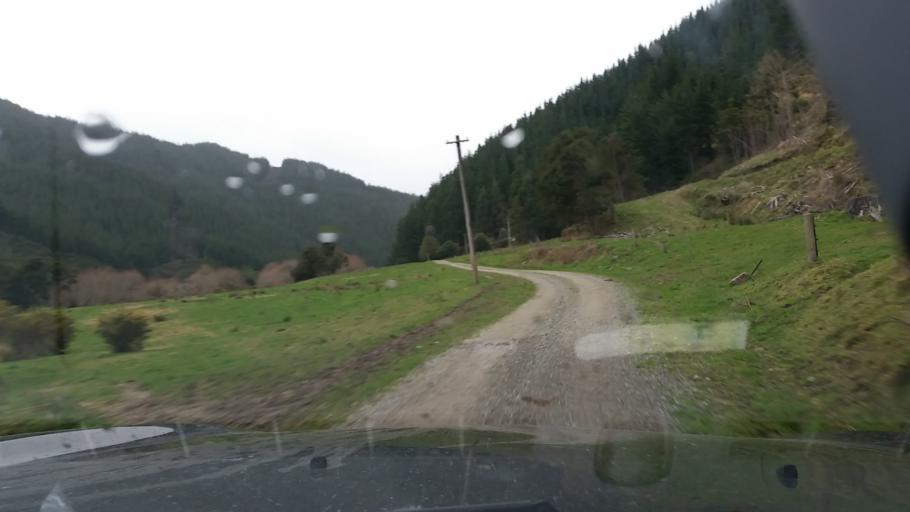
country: NZ
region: Marlborough
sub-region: Marlborough District
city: Blenheim
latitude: -41.3897
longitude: 173.8490
